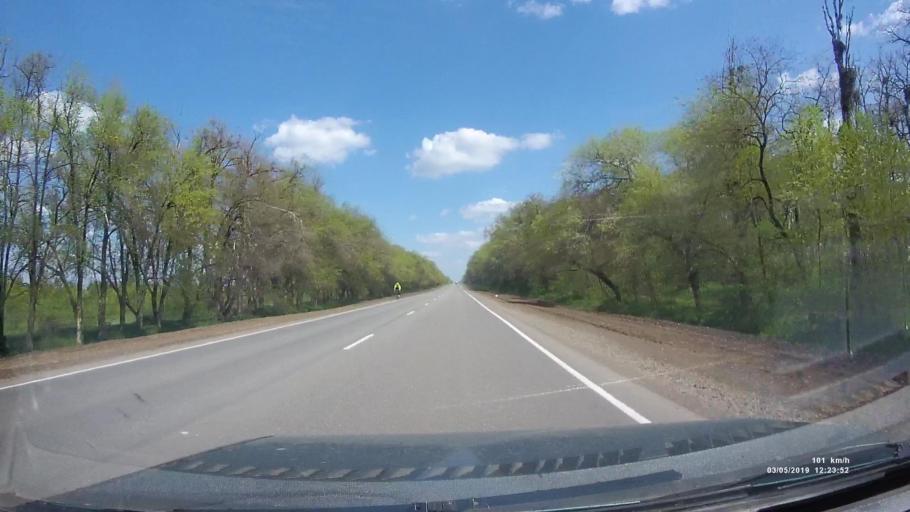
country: RU
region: Rostov
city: Semikarakorsk
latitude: 47.4138
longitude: 40.6902
